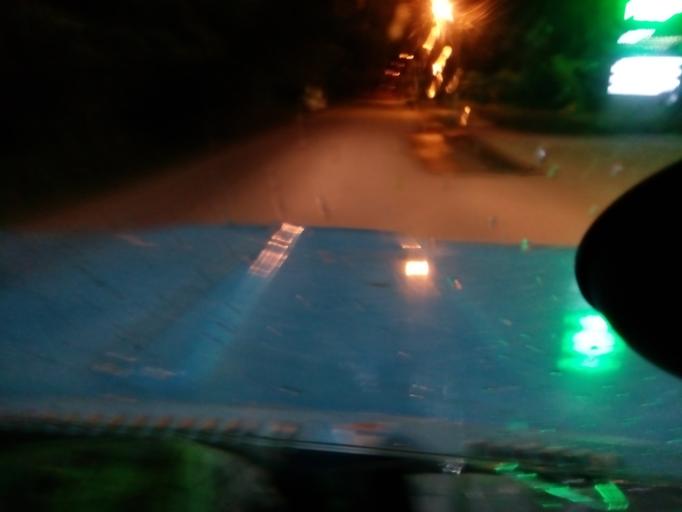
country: CO
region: Boyaca
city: Puerto Boyaca
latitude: 5.9720
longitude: -74.5736
